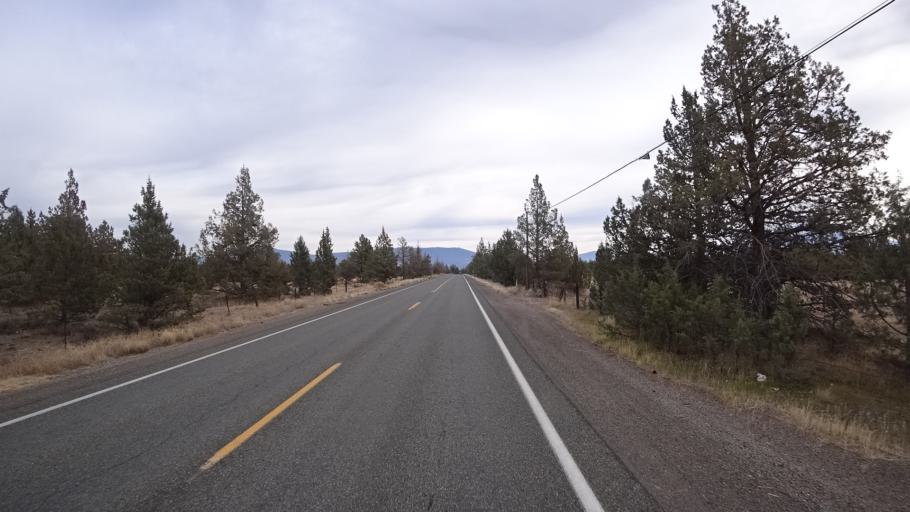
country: US
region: California
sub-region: Siskiyou County
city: Montague
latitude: 41.6347
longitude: -122.4430
